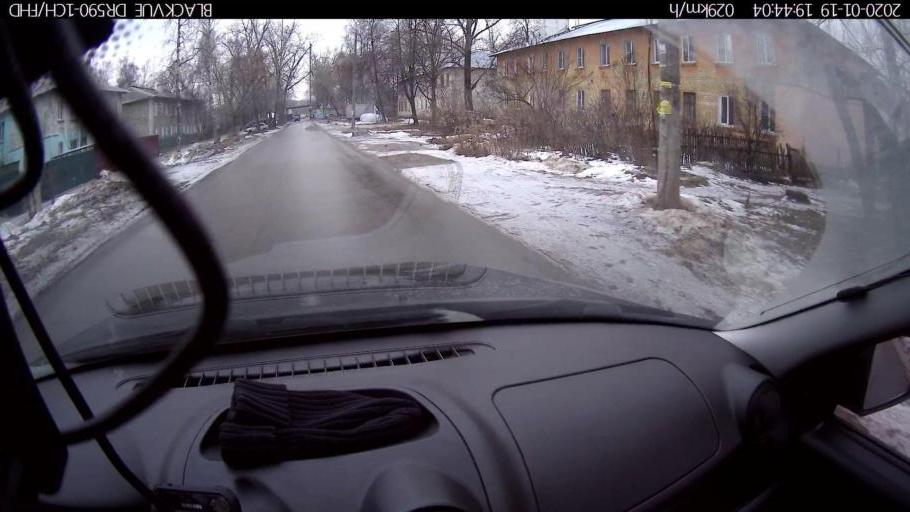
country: RU
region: Nizjnij Novgorod
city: Nizhniy Novgorod
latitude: 56.3003
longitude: 43.9119
